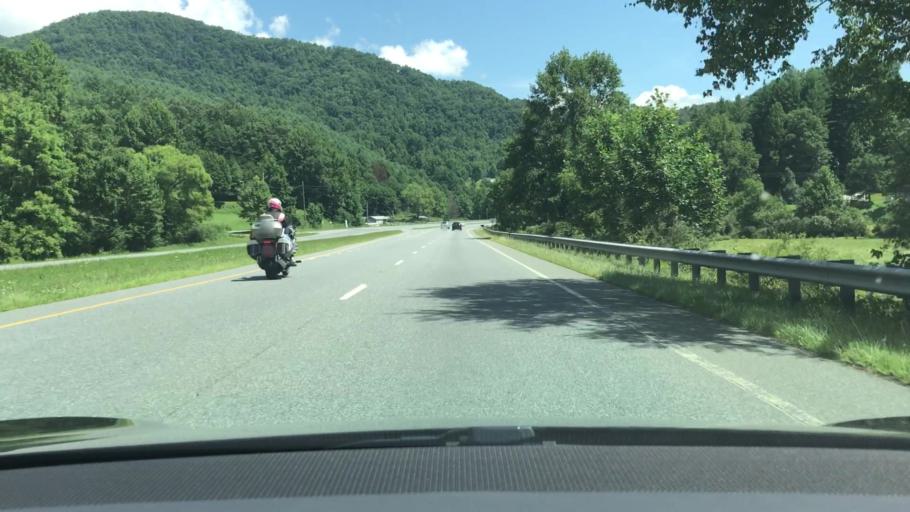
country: US
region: North Carolina
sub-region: Jackson County
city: Sylva
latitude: 35.2872
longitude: -83.2837
